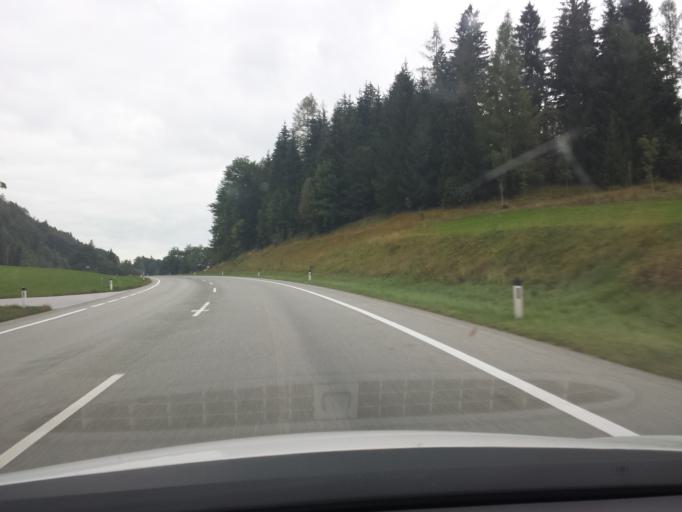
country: AT
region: Salzburg
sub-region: Politischer Bezirk Salzburg-Umgebung
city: Fuschl am See
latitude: 47.7949
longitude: 13.2819
